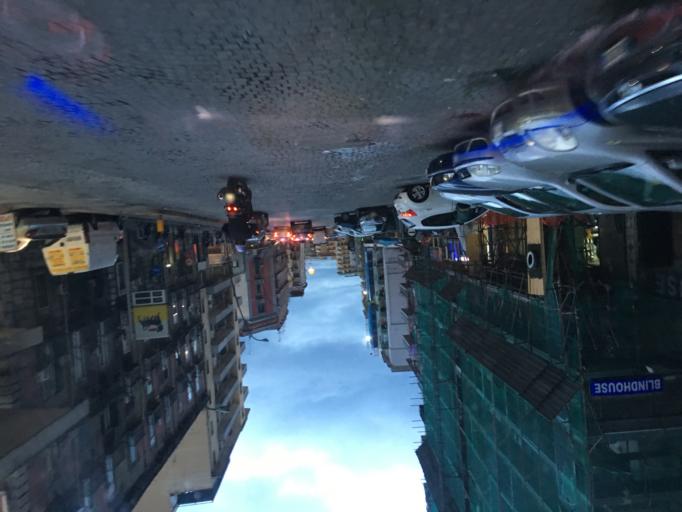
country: IT
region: Campania
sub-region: Provincia di Napoli
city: Bagnoli
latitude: 40.8280
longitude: 14.2087
